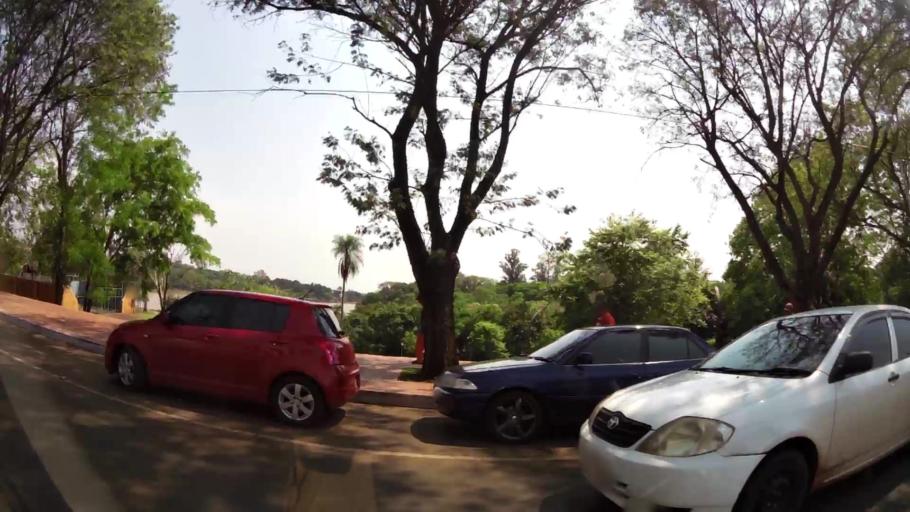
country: PY
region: Alto Parana
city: Ciudad del Este
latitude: -25.5192
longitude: -54.6189
